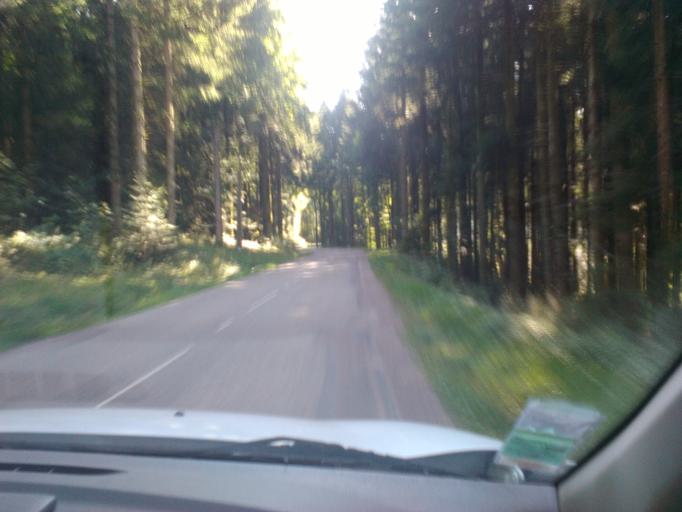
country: FR
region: Lorraine
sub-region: Departement des Vosges
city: Le Tholy
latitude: 48.0838
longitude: 6.7946
